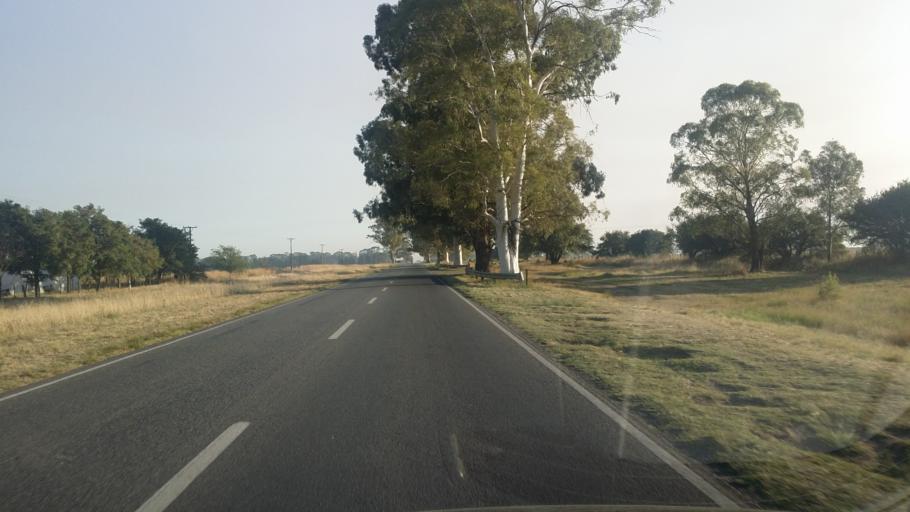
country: AR
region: La Pampa
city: Santa Rosa
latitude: -36.5478
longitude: -64.2807
